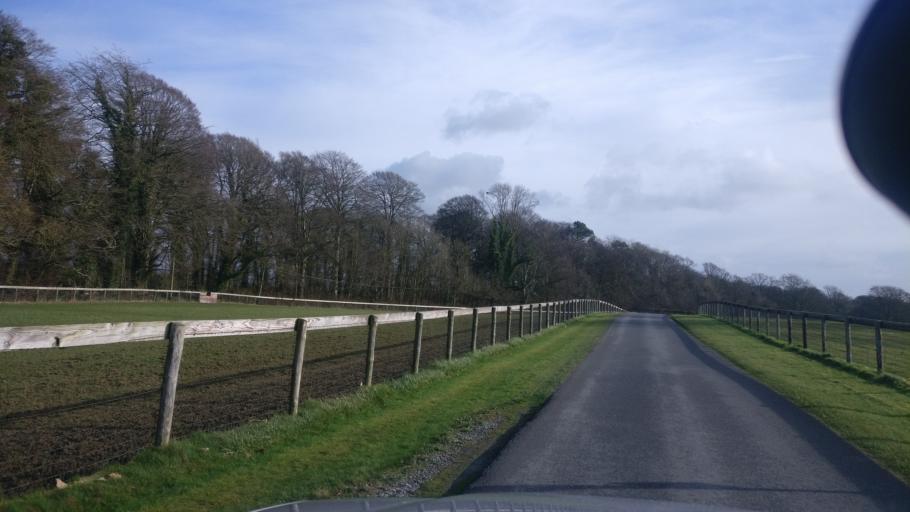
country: IE
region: Leinster
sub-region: Kilkenny
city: Thomastown
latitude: 52.5327
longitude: -7.1754
